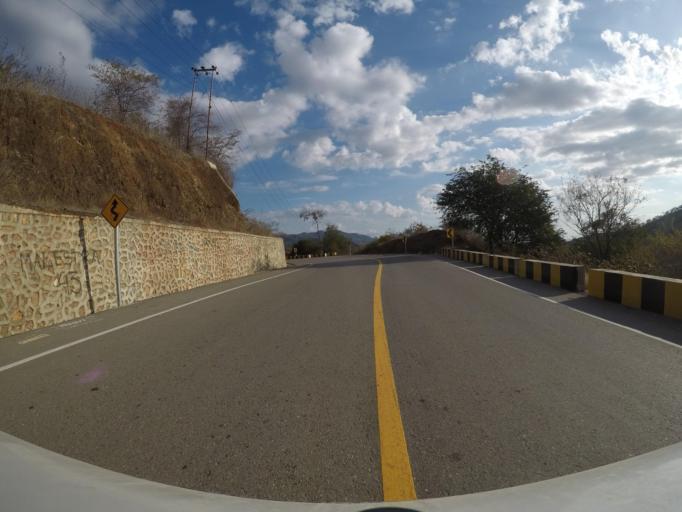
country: TL
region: Bobonaro
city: Maliana
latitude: -8.8550
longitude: 125.0562
